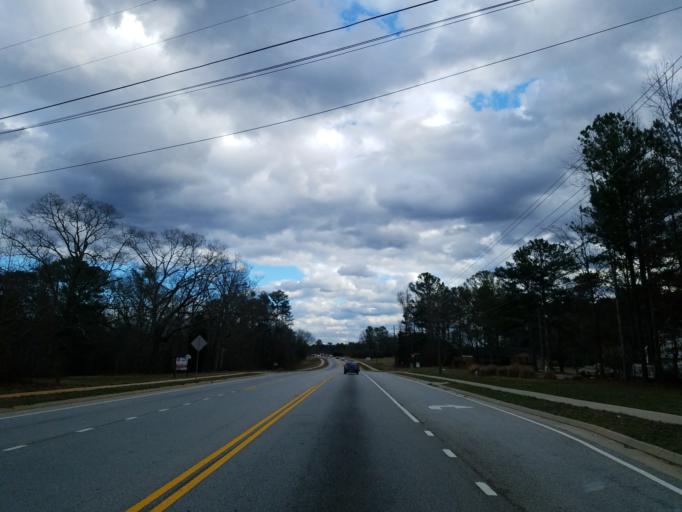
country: US
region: Georgia
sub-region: Henry County
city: McDonough
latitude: 33.4333
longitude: -84.1132
